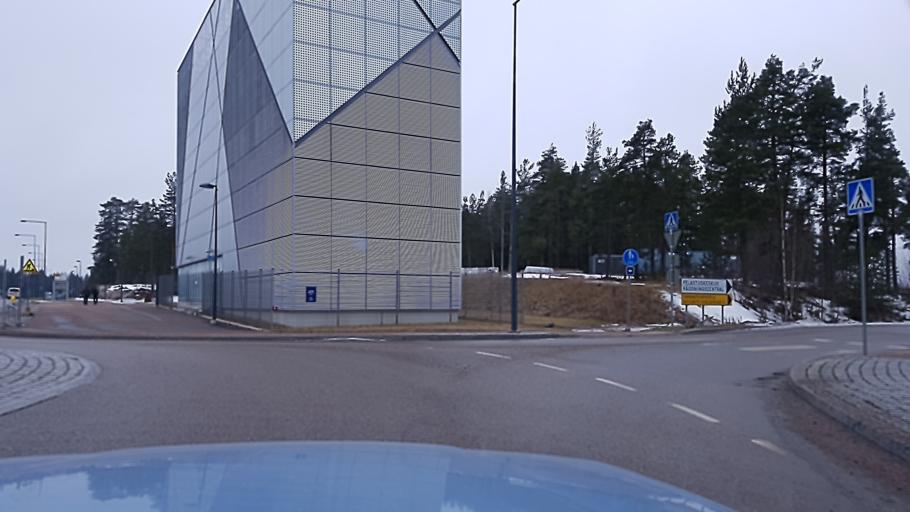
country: FI
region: Uusimaa
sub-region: Helsinki
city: Vantaa
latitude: 60.3056
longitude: 24.9580
